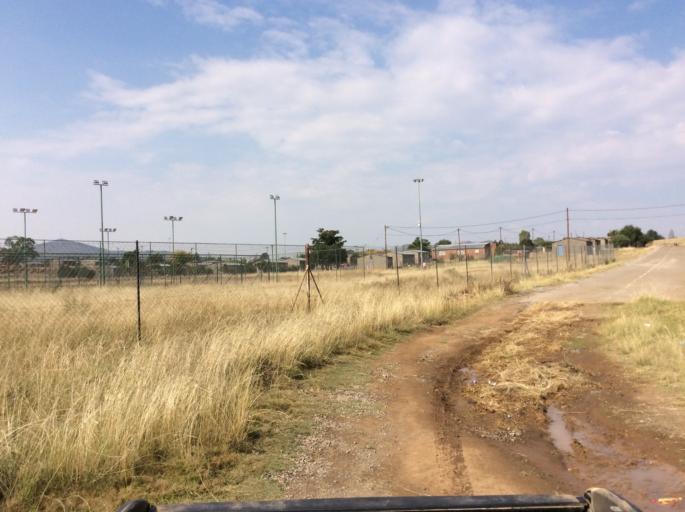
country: LS
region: Mafeteng
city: Mafeteng
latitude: -29.9846
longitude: 27.0065
